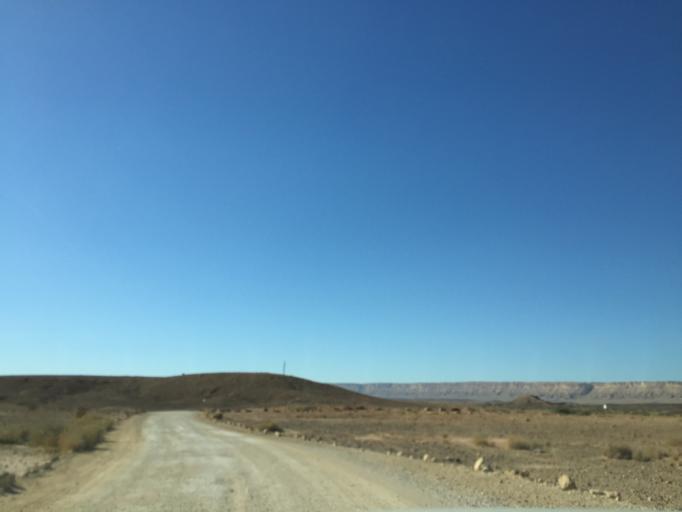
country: IL
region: Southern District
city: Mitzpe Ramon
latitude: 30.6245
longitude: 34.9224
